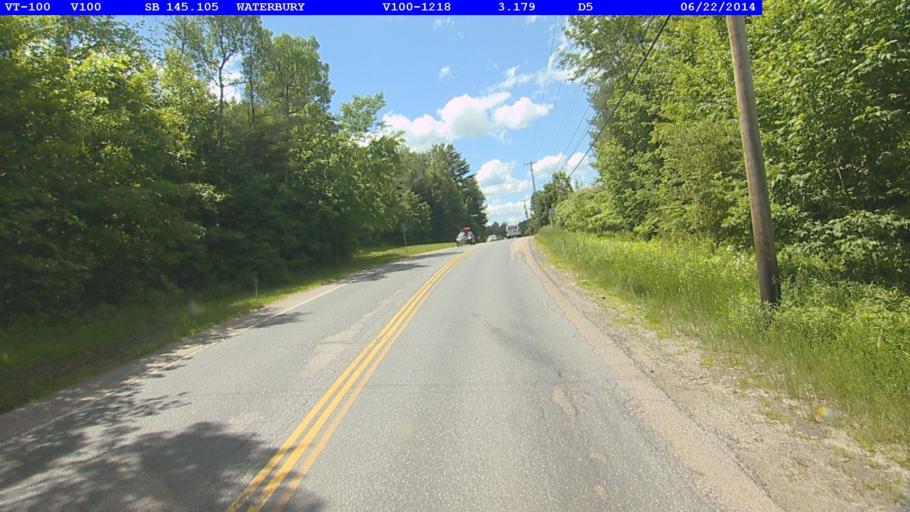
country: US
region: Vermont
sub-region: Washington County
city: Waterbury
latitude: 44.3762
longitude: -72.7254
